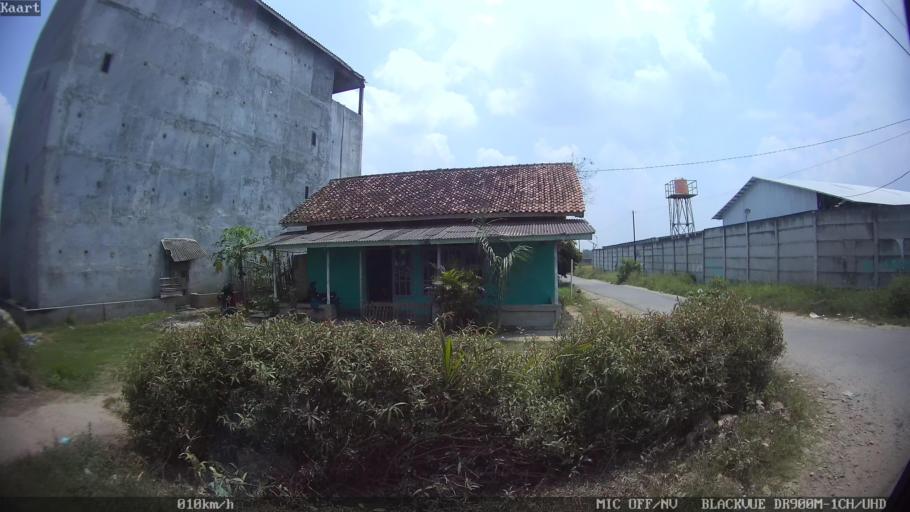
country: ID
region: Lampung
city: Pringsewu
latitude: -5.3550
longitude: 104.9941
